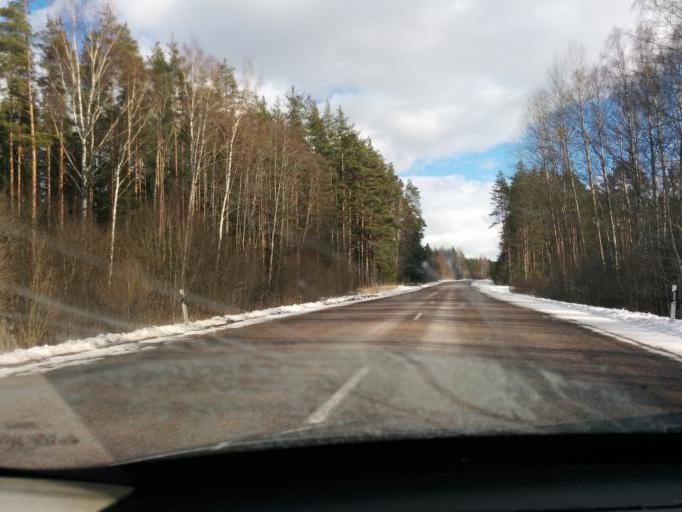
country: LV
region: Gulbenes Rajons
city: Gulbene
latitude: 57.2295
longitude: 26.5308
